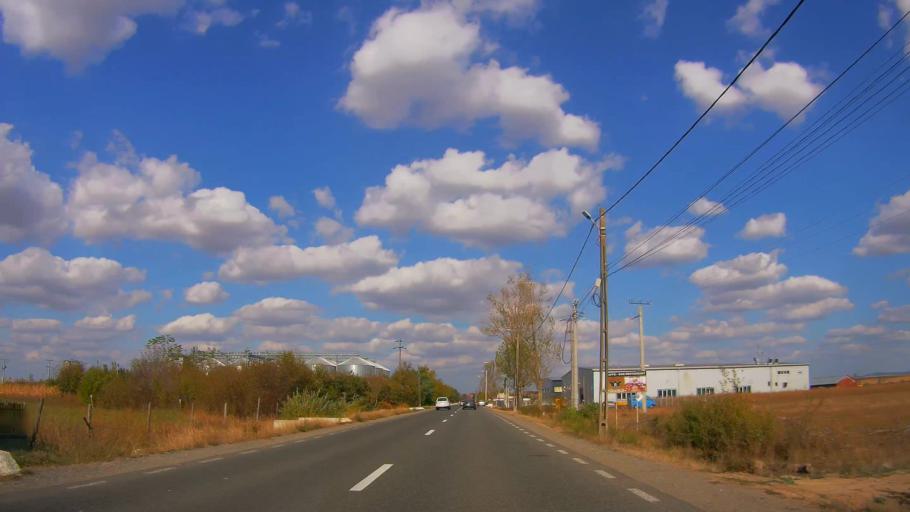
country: RO
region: Satu Mare
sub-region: Oras Ardud
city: Ardud
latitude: 47.6239
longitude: 22.8716
